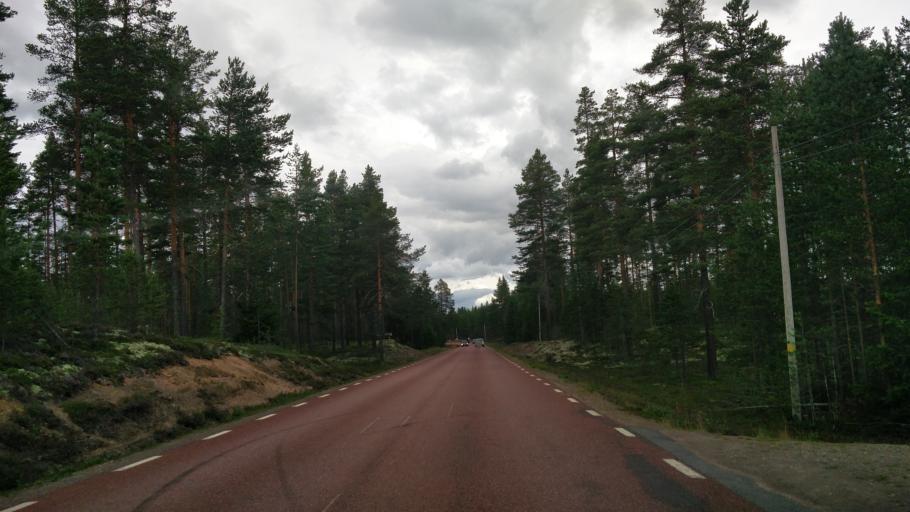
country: NO
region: Hedmark
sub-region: Trysil
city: Innbygda
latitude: 61.1404
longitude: 12.8074
